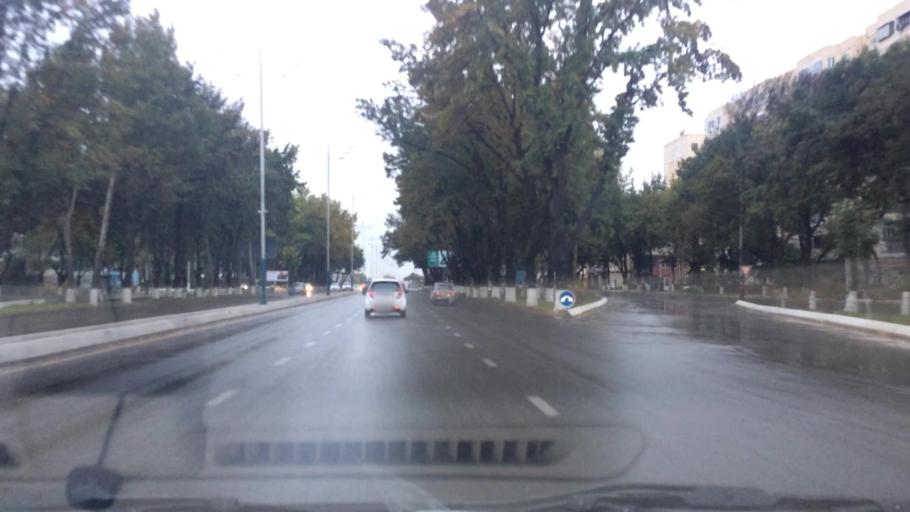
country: UZ
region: Toshkent Shahri
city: Tashkent
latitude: 41.2968
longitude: 69.2285
